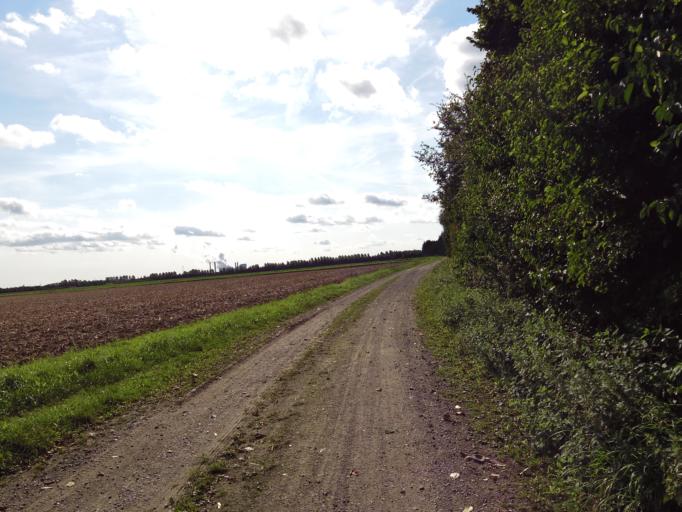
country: DE
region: North Rhine-Westphalia
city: Niedermerz
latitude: 50.8574
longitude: 6.2497
